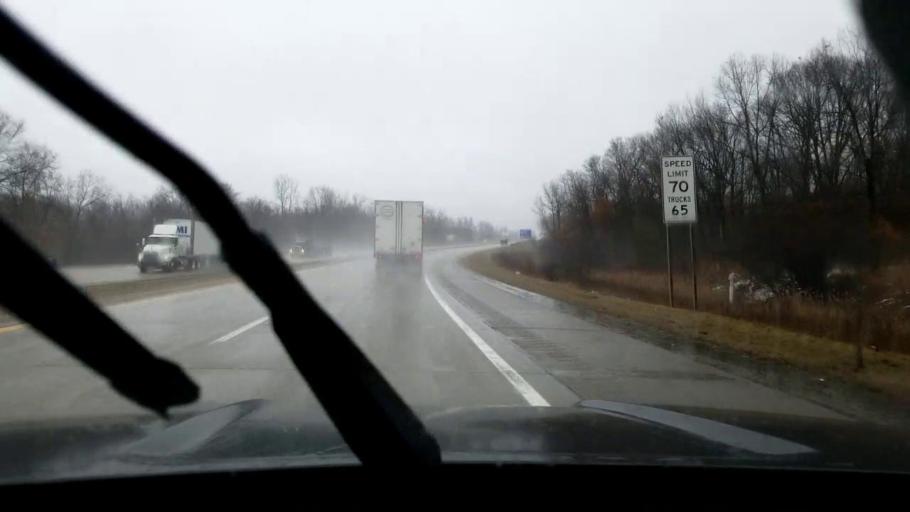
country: US
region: Michigan
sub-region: Jackson County
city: Michigan Center
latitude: 42.2289
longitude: -84.3621
